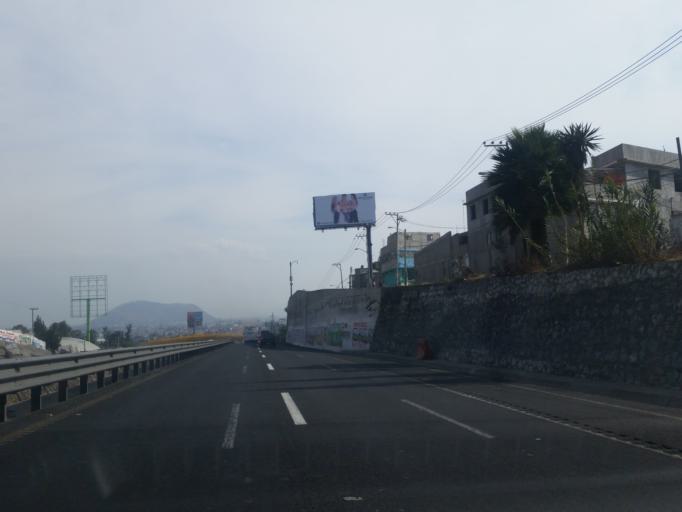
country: MX
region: Mexico
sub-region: La Paz
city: Emiliano Zapata
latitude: 19.3318
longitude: -98.9683
